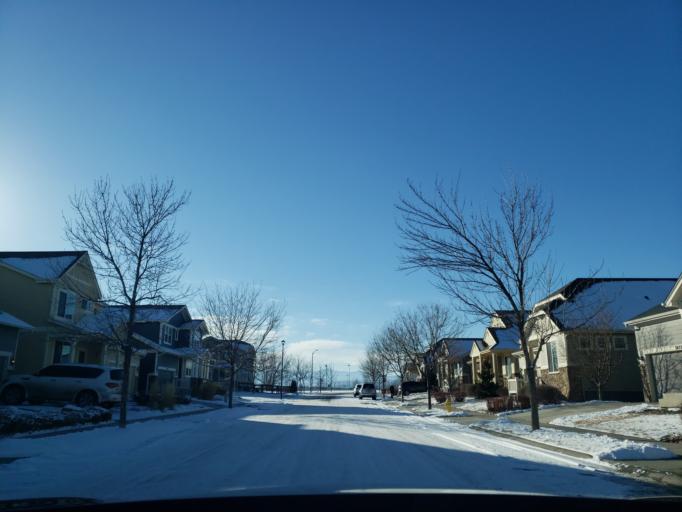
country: US
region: Colorado
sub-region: Larimer County
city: Fort Collins
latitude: 40.5116
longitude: -105.0090
